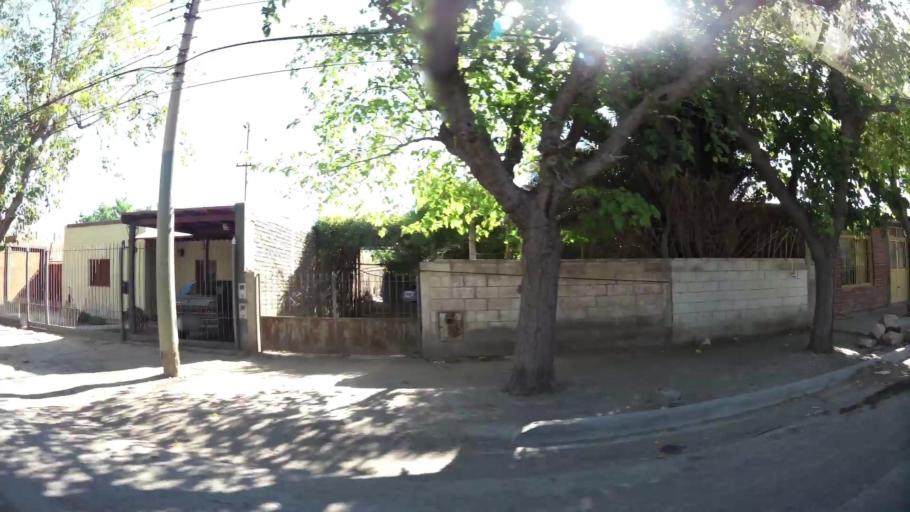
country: AR
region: San Juan
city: Villa Paula de Sarmiento
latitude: -31.5114
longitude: -68.5247
